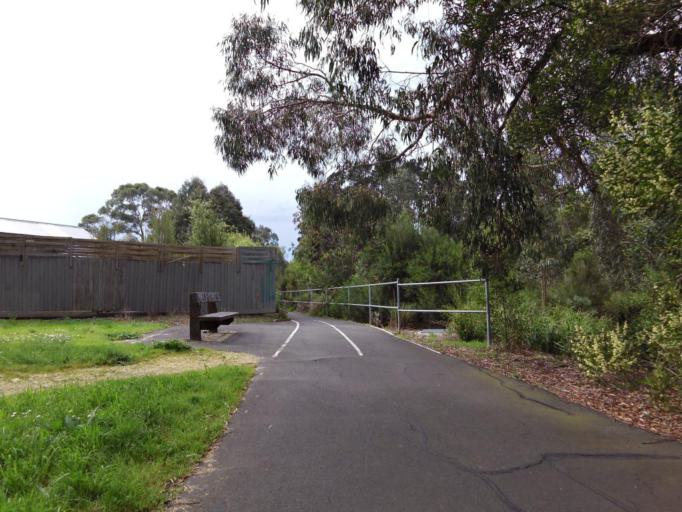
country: AU
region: Victoria
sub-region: Maroondah
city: Croydon Hills
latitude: -37.7909
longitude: 145.2573
